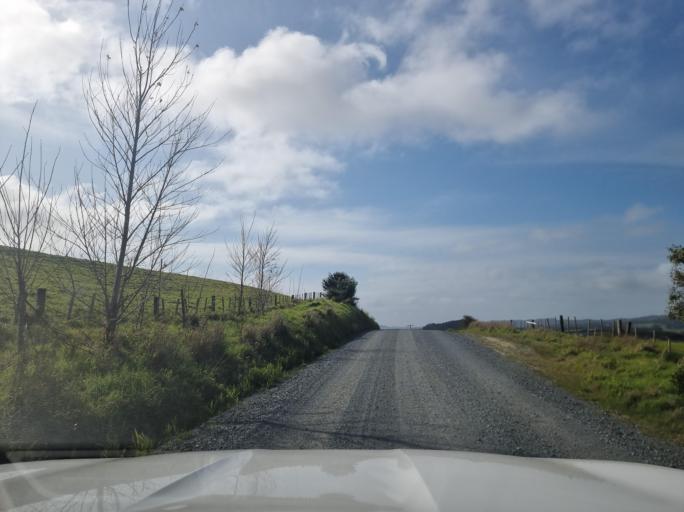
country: NZ
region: Northland
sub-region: Whangarei
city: Ruakaka
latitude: -36.0117
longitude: 174.4753
